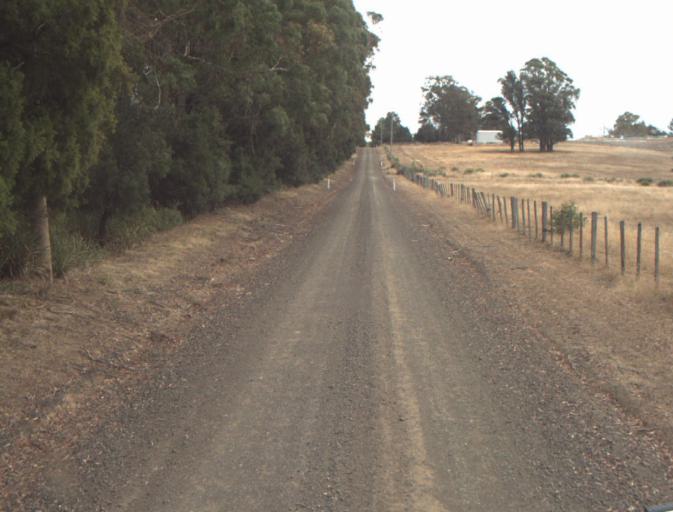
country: AU
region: Tasmania
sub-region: Launceston
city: Mayfield
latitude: -41.2774
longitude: 147.0466
